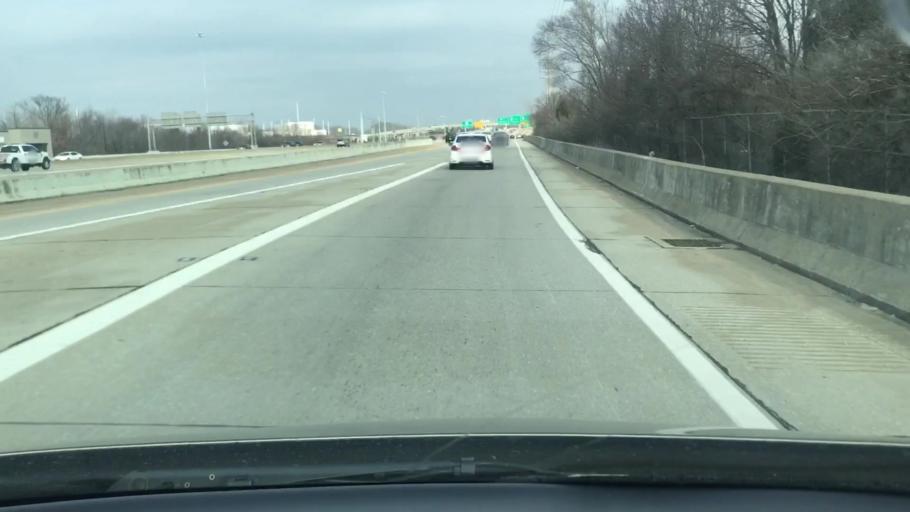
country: US
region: Kentucky
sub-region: Jefferson County
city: Saint Regis Park
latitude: 38.2412
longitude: -85.6216
